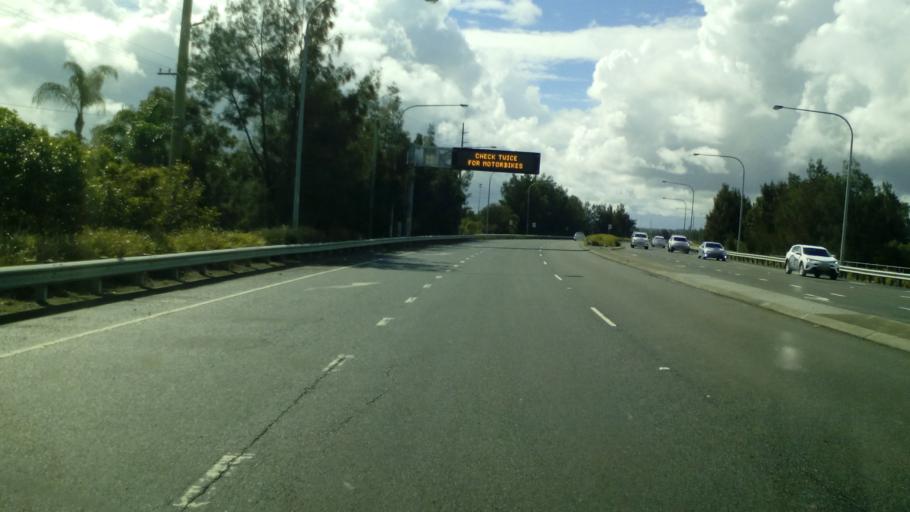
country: AU
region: New South Wales
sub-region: Lake Macquarie Shire
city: Fennell Bay
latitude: -32.9654
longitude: 151.6080
